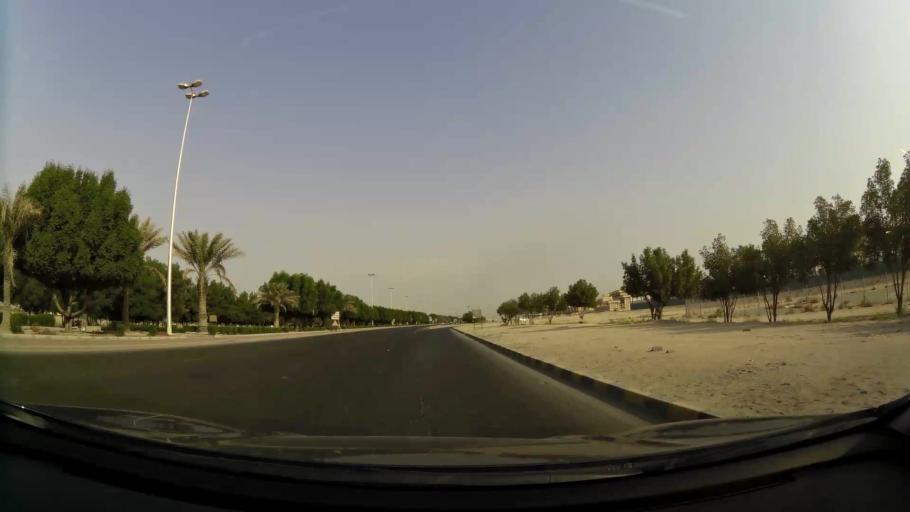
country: KW
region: Al Asimah
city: Ar Rabiyah
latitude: 29.3266
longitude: 47.8000
